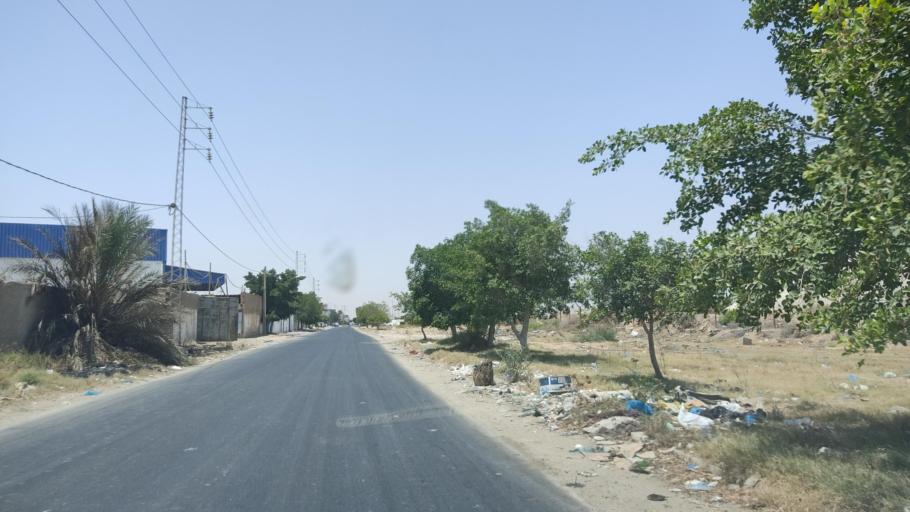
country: TN
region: Safaqis
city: Sfax
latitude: 34.6930
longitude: 10.7264
